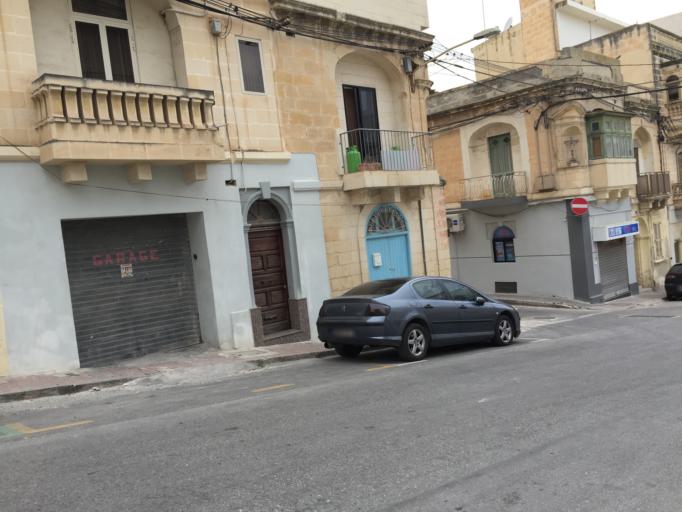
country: MT
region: Tal-Pieta
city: Pieta
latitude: 35.8938
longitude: 14.4925
